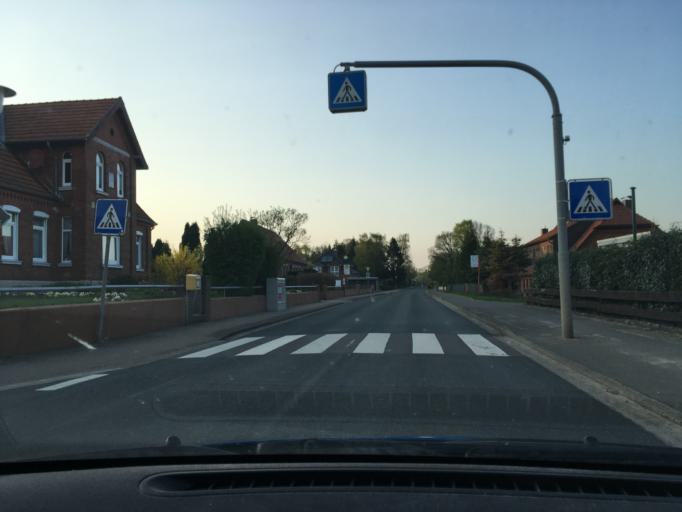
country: DE
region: Lower Saxony
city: Sudergellersen
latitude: 53.2127
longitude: 10.2976
